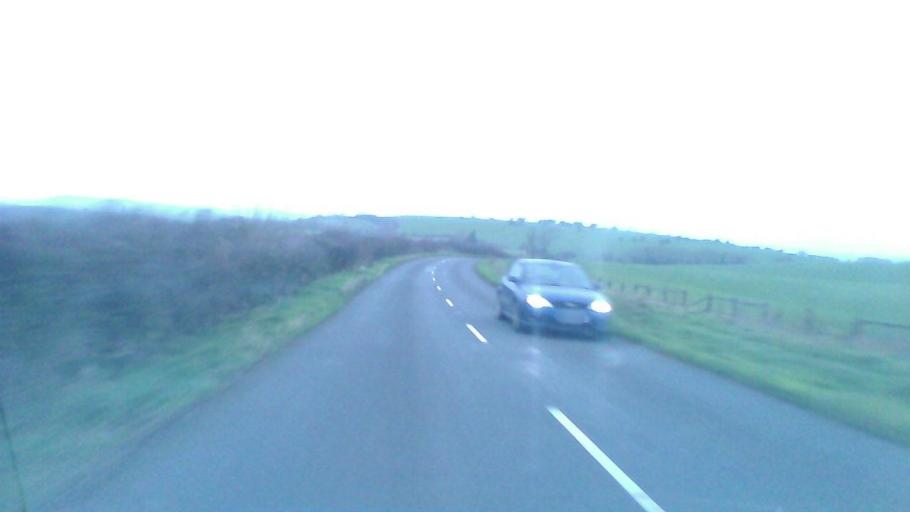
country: GB
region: England
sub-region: Isle of Wight
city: Brading
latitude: 50.6796
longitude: -1.1747
